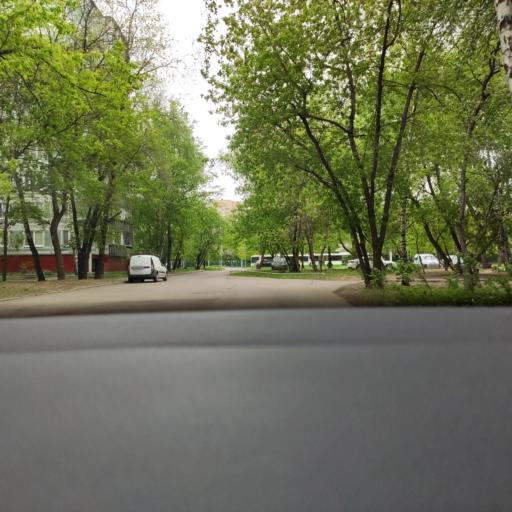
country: RU
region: Moscow
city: Otradnoye
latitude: 55.8697
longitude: 37.6066
